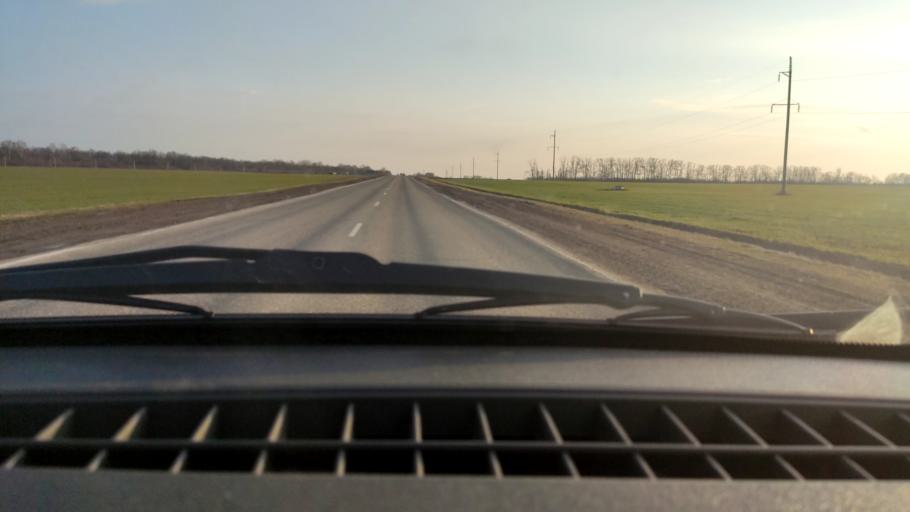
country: RU
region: Bashkortostan
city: Chishmy
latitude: 54.5561
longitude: 55.3379
